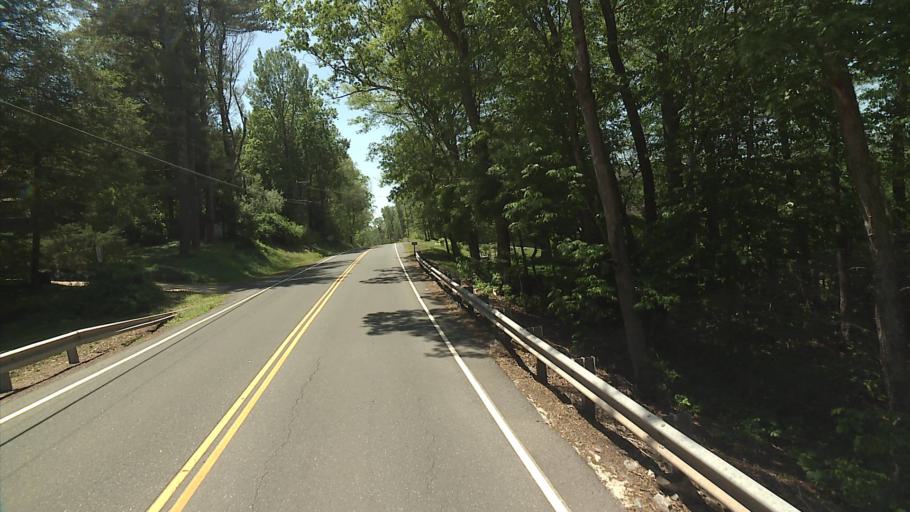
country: US
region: Massachusetts
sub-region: Hampden County
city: Wales
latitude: 42.0227
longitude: -72.2477
